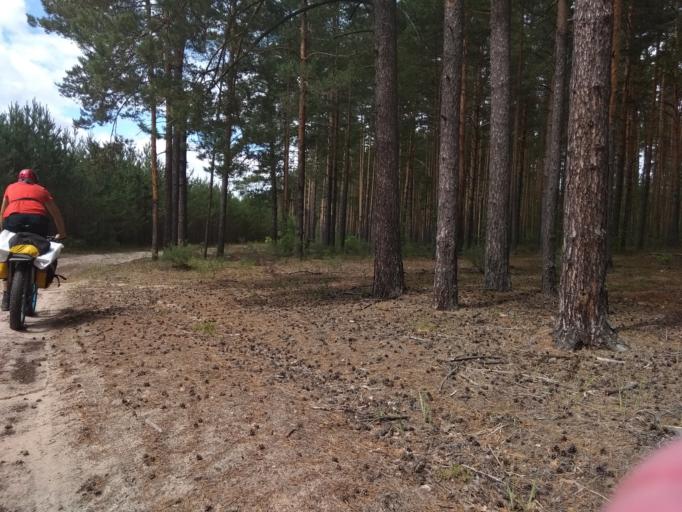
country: RU
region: Moskovskaya
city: Misheronskiy
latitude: 55.6398
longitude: 39.7086
